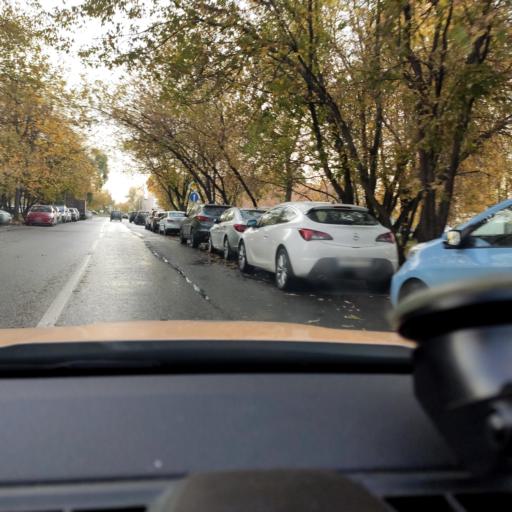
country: RU
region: Moscow
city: Vatutino
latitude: 55.8563
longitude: 37.6885
